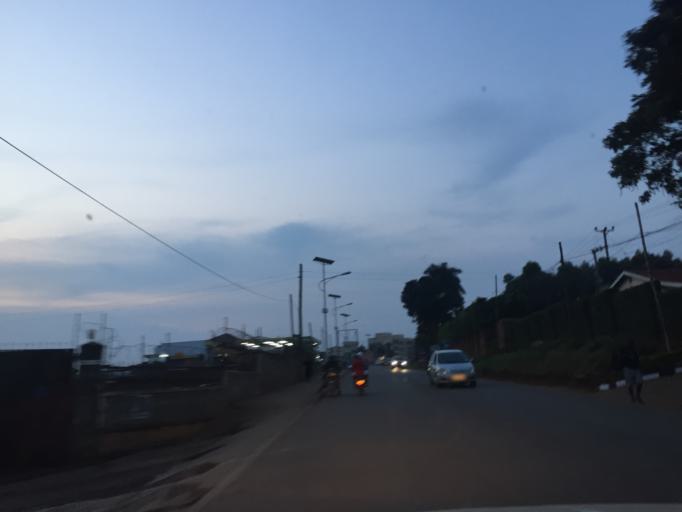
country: UG
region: Central Region
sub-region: Kampala District
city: Kampala
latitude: 0.3002
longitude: 32.6027
